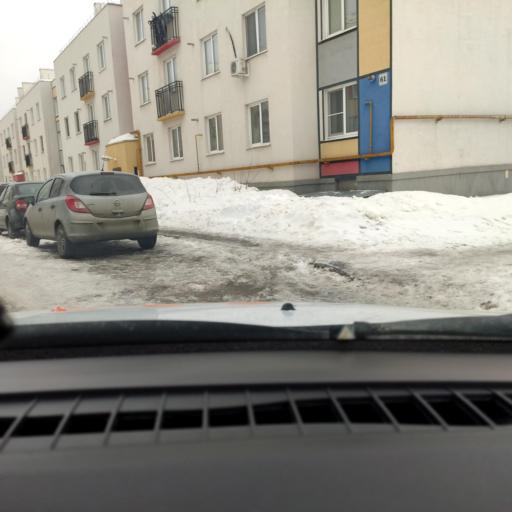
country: RU
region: Samara
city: Petra-Dubrava
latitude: 53.3234
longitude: 50.3161
